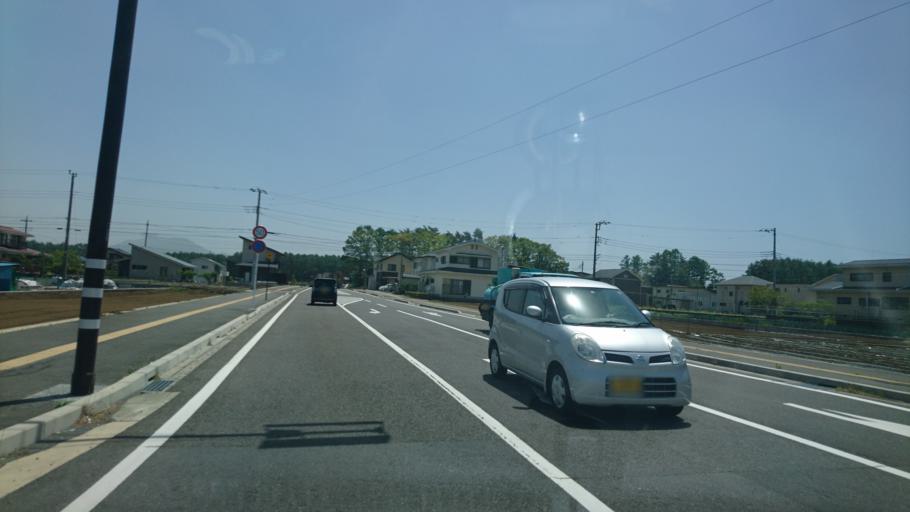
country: JP
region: Yamanashi
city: Fujikawaguchiko
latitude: 35.4966
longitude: 138.7395
